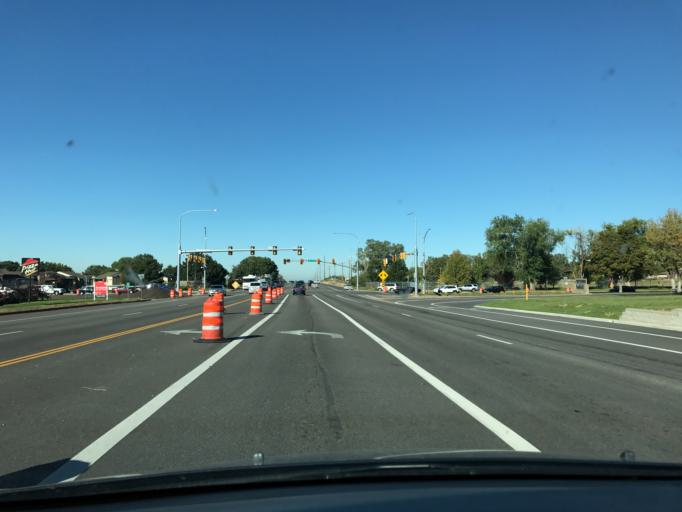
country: US
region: Utah
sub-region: Davis County
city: Hill Air Force Bace
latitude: 41.1035
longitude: -111.9722
